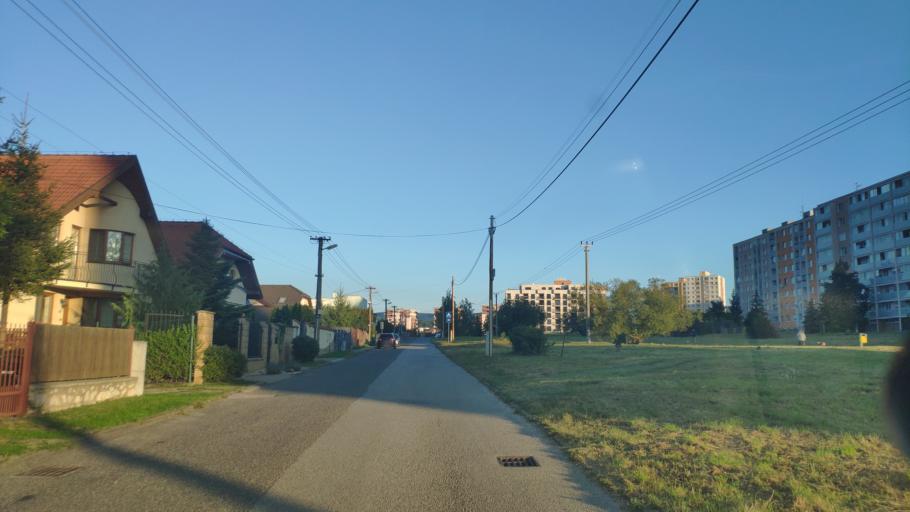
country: SK
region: Kosicky
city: Kosice
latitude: 48.7089
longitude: 21.2110
